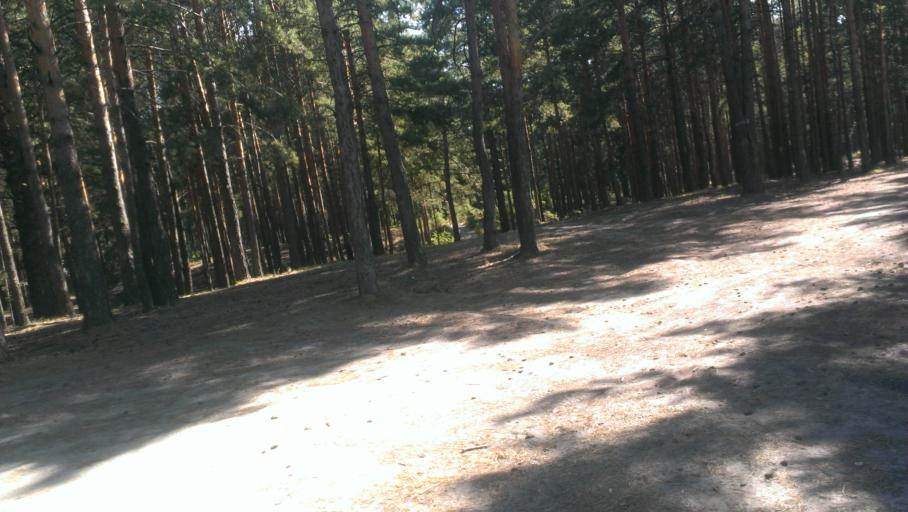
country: RU
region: Altai Krai
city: Novosilikatnyy
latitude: 53.3195
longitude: 83.6855
